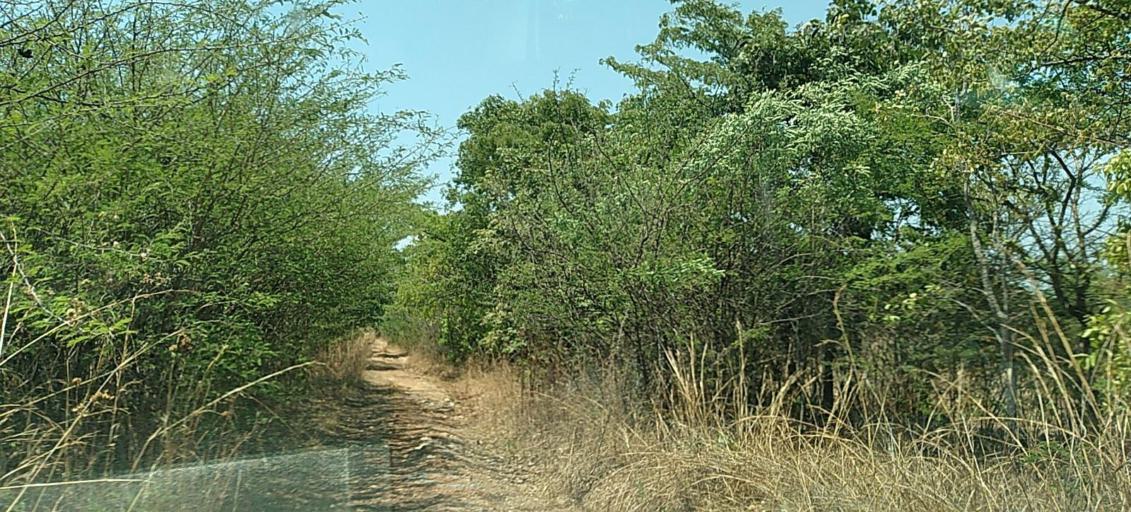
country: ZM
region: Copperbelt
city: Luanshya
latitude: -12.9888
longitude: 28.3259
